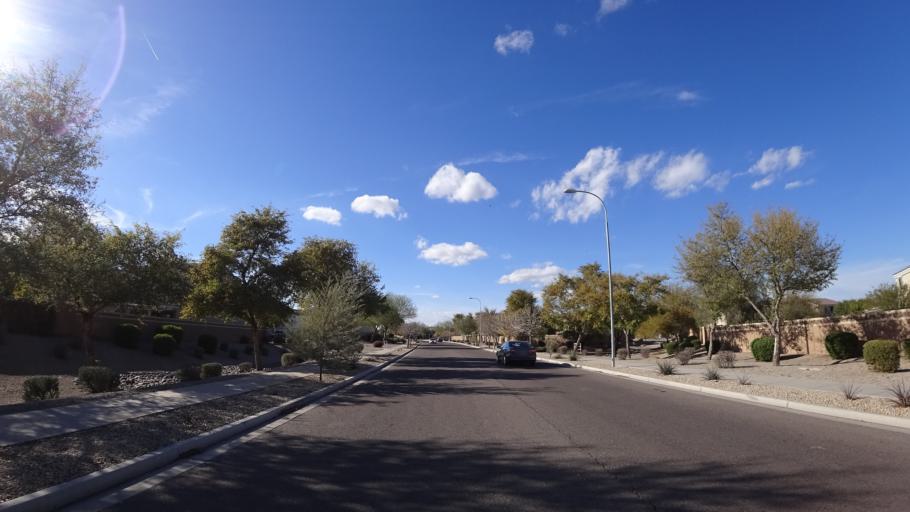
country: US
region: Arizona
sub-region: Maricopa County
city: Tolleson
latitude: 33.4191
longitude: -112.2437
